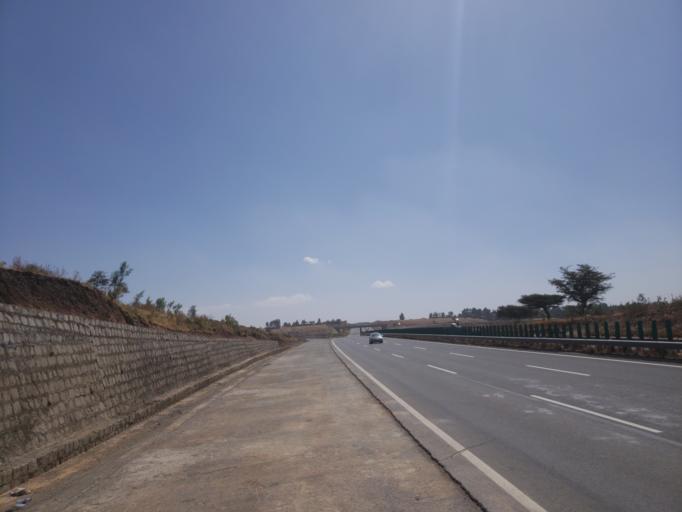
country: ET
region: Oromiya
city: Mojo
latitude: 8.5829
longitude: 39.1690
